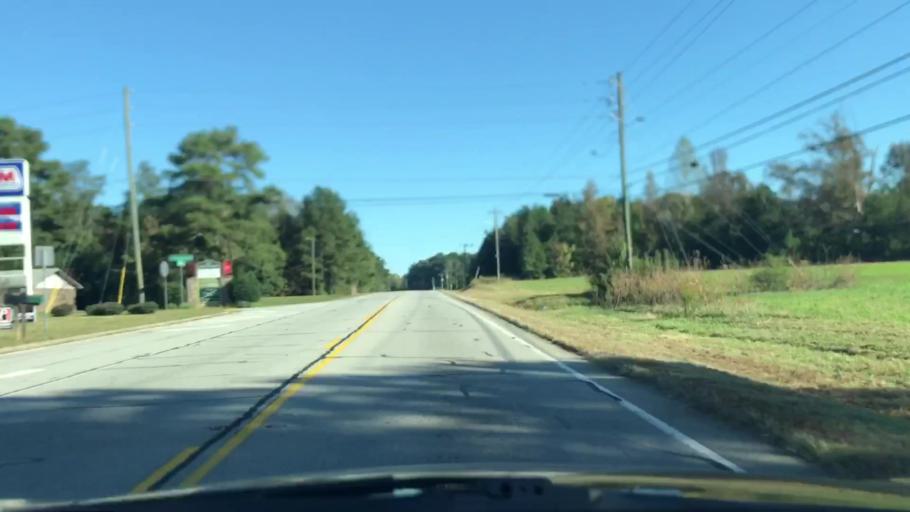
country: US
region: Georgia
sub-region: Carroll County
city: Villa Rica
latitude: 33.7909
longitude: -84.8944
